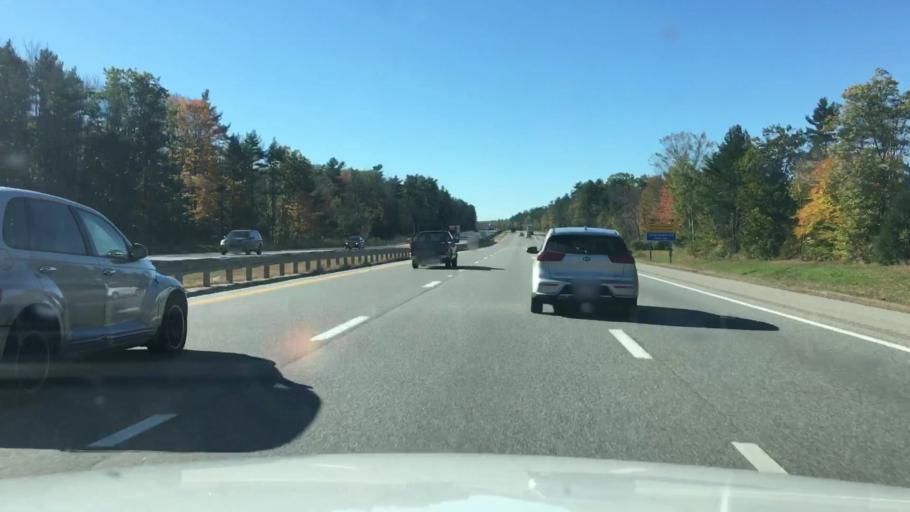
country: US
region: Maine
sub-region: York County
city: West Kennebunk
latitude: 43.4317
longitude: -70.5464
